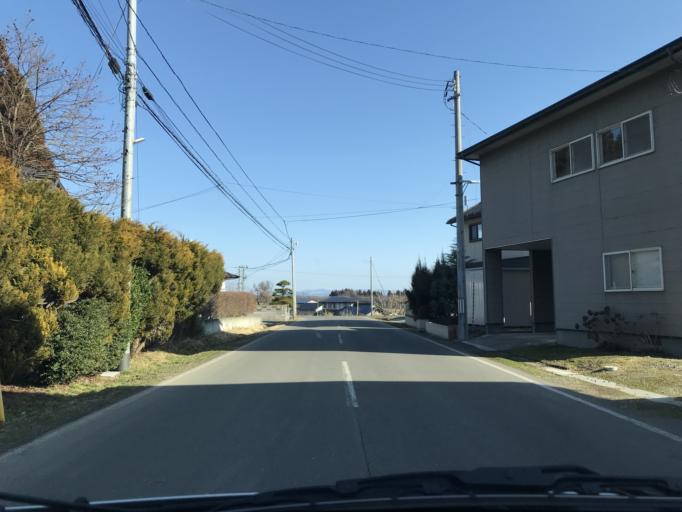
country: JP
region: Iwate
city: Kitakami
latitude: 39.2948
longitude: 141.0467
